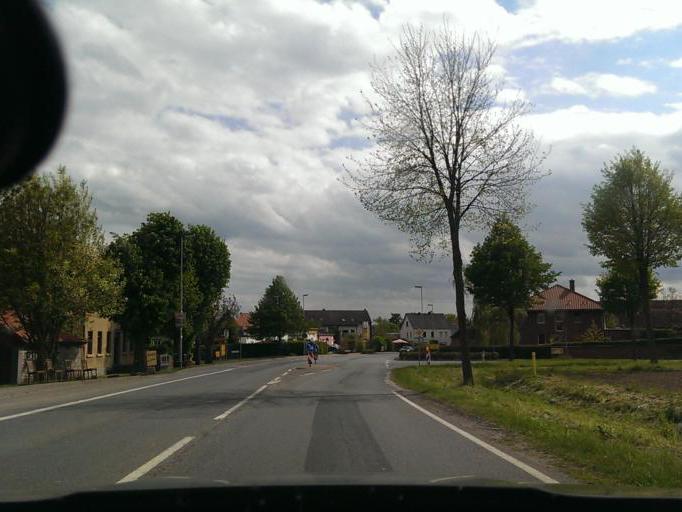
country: DE
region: Lower Saxony
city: Elze
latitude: 52.1534
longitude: 9.7392
